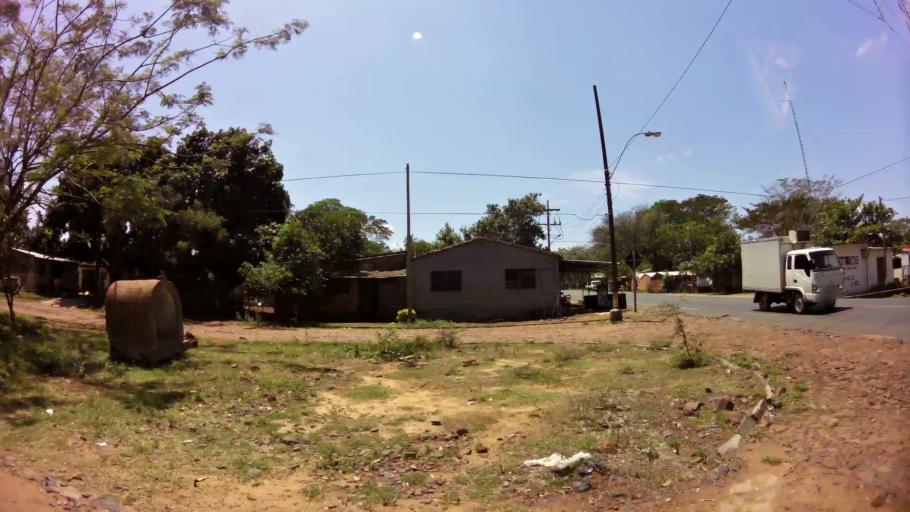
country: PY
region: Central
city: San Antonio
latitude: -25.4144
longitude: -57.5545
